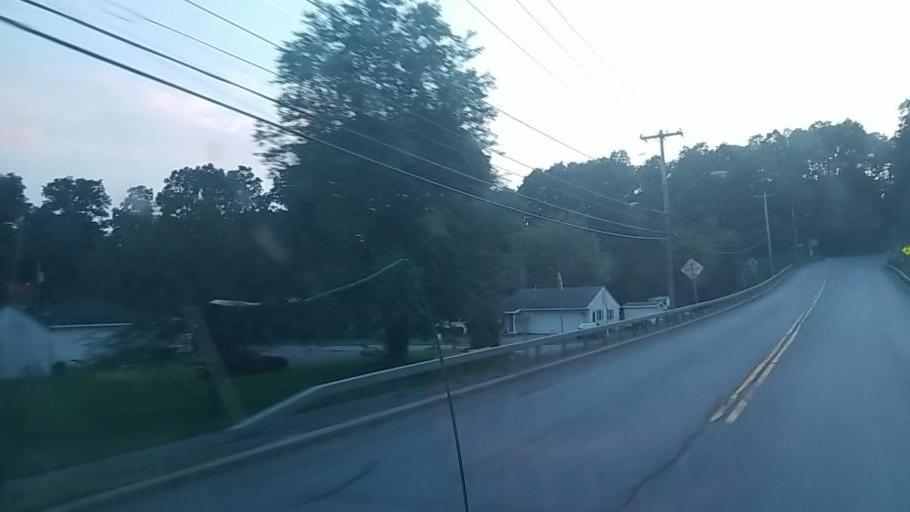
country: US
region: New York
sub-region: Montgomery County
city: Fonda
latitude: 42.9575
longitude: -74.3809
